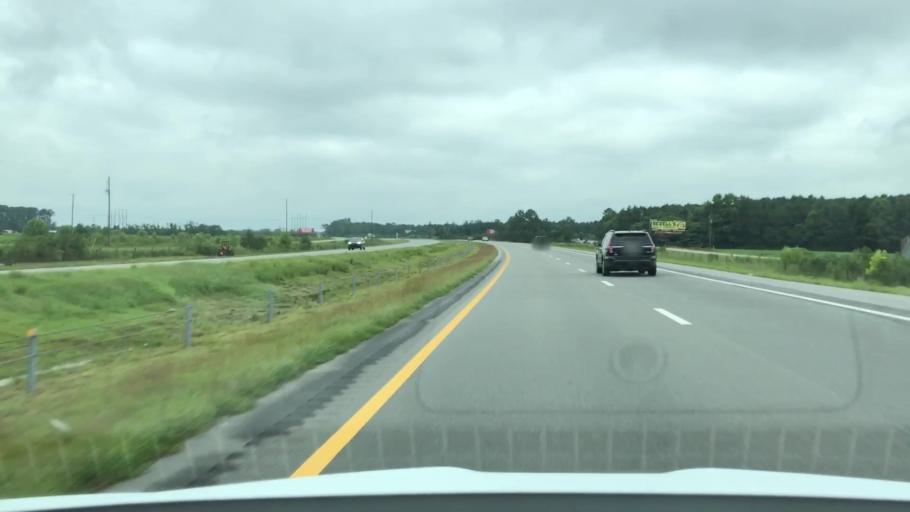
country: US
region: North Carolina
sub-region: Wayne County
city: Elroy
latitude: 35.3936
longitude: -77.8672
